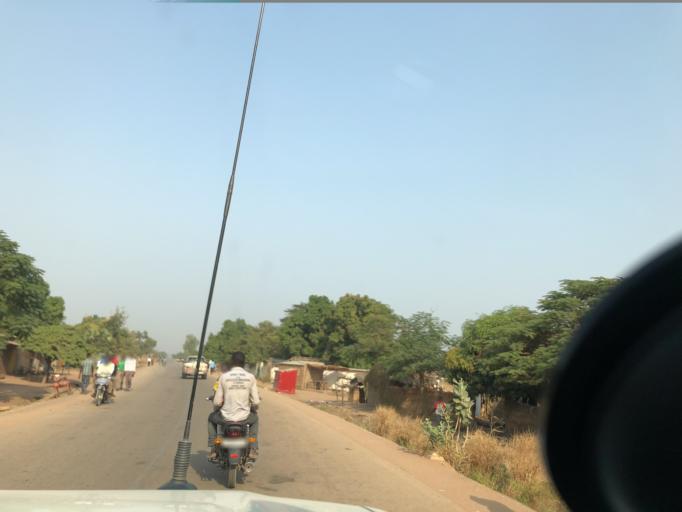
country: TD
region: Logone Occidental
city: Moundou
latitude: 8.5659
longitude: 16.0530
